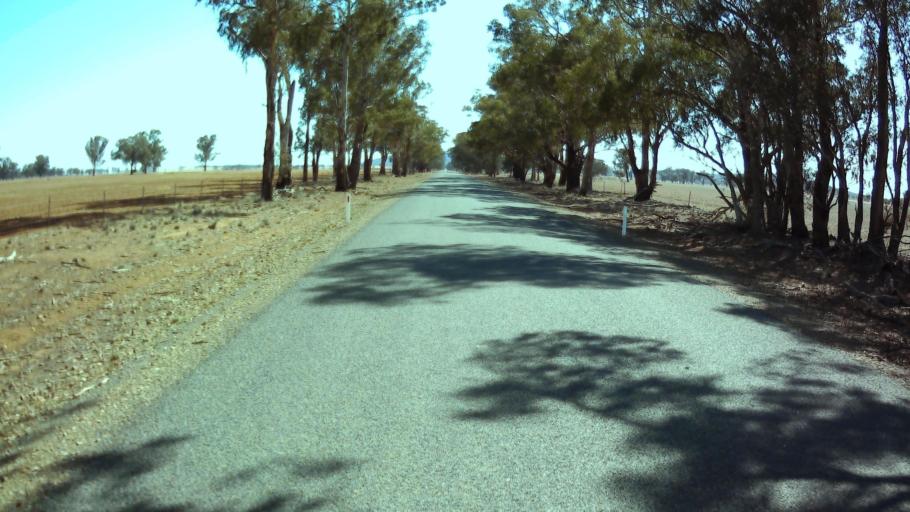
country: AU
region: New South Wales
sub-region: Weddin
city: Grenfell
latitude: -33.7194
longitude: 147.9014
